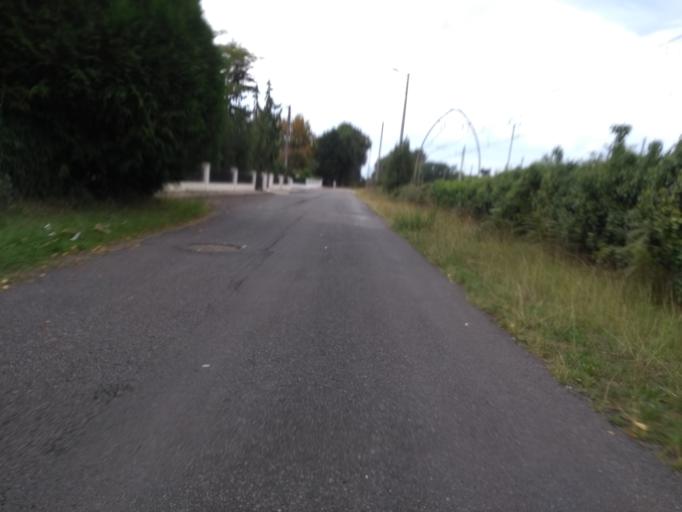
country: FR
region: Aquitaine
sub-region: Departement de la Gironde
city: Saint-Aubin-de-Medoc
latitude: 44.7694
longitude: -0.7041
